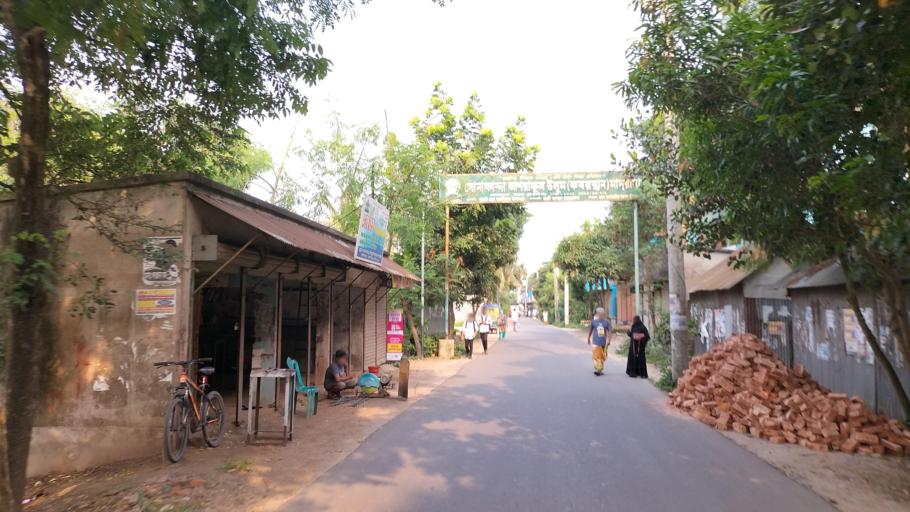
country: BD
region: Dhaka
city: Azimpur
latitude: 23.6678
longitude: 90.3245
